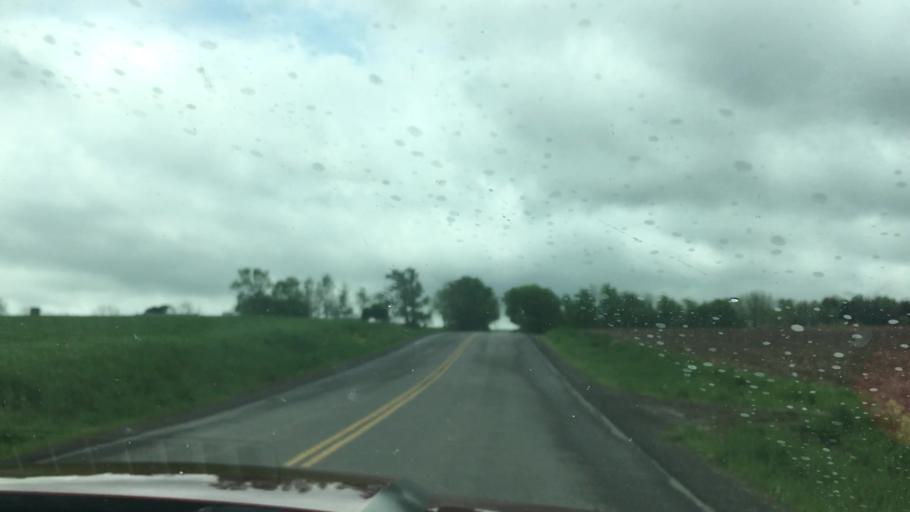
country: US
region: New York
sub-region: Genesee County
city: Batavia
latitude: 43.0877
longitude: -78.1392
